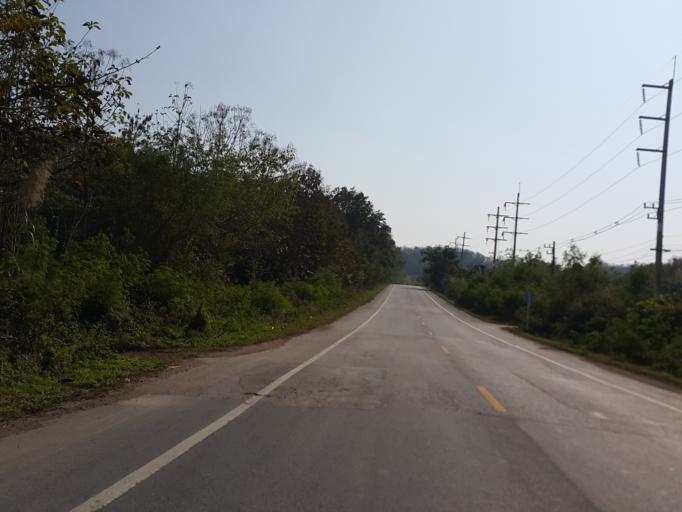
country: TH
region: Lampang
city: Chae Hom
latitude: 18.6203
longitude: 99.5441
